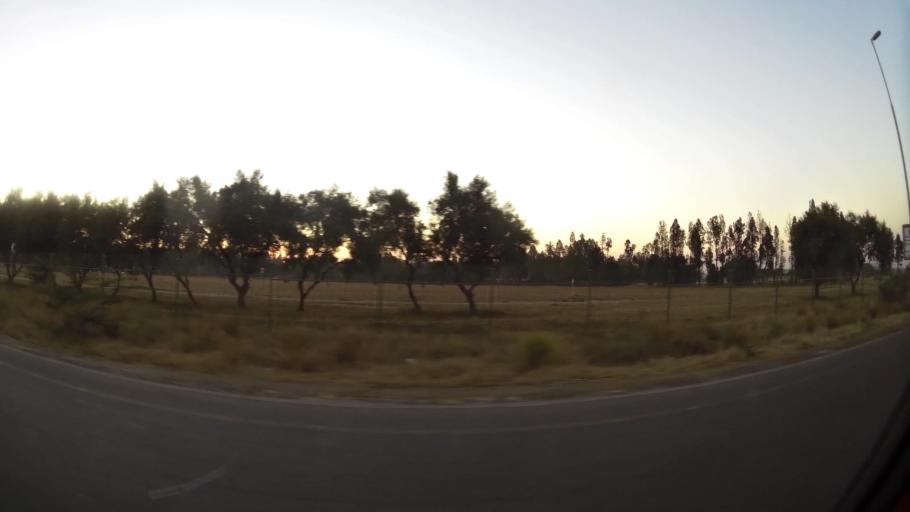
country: ZA
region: North-West
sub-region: Bojanala Platinum District Municipality
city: Rustenburg
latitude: -25.6430
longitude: 27.2613
